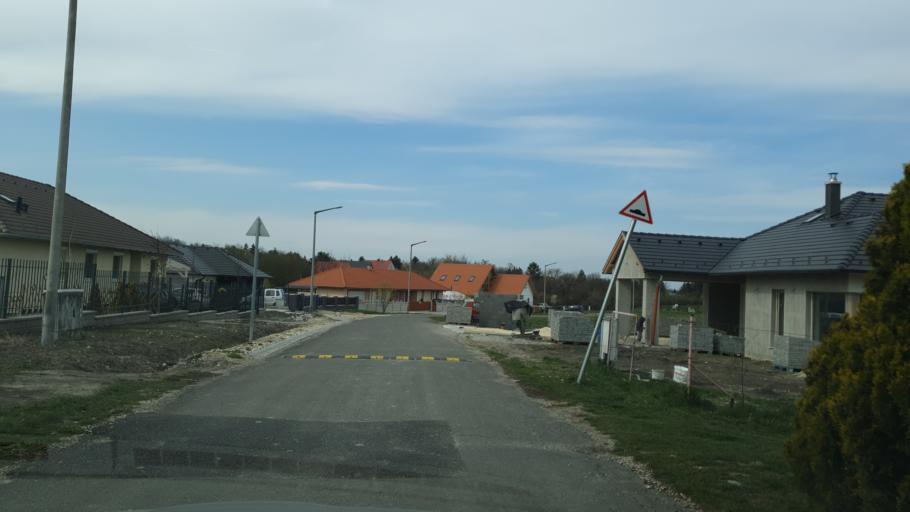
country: HU
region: Fejer
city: Etyek
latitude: 47.4388
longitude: 18.7500
